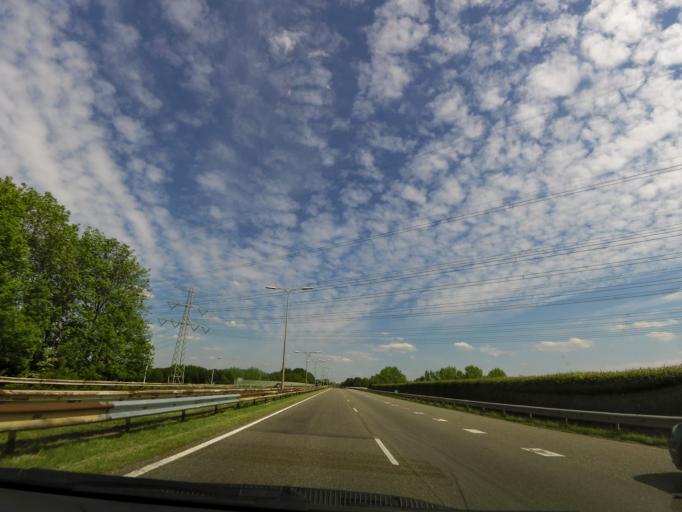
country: NL
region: Limburg
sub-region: Gemeente Leudal
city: Haelen
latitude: 51.2033
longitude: 5.9500
